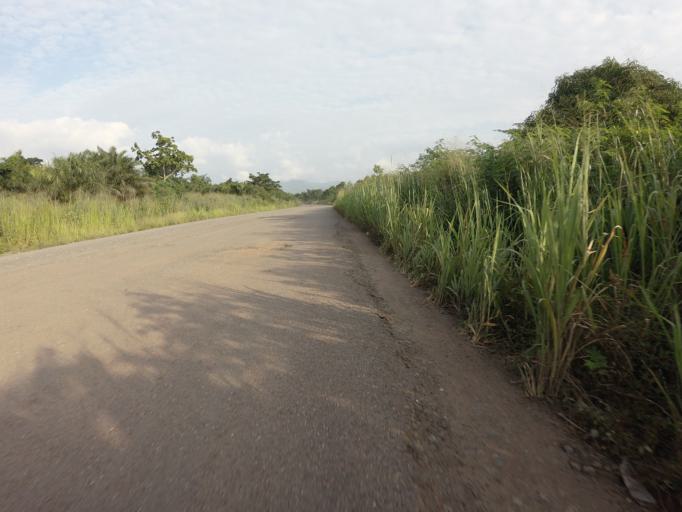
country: GH
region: Volta
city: Kpandu
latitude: 6.9798
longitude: 0.4482
